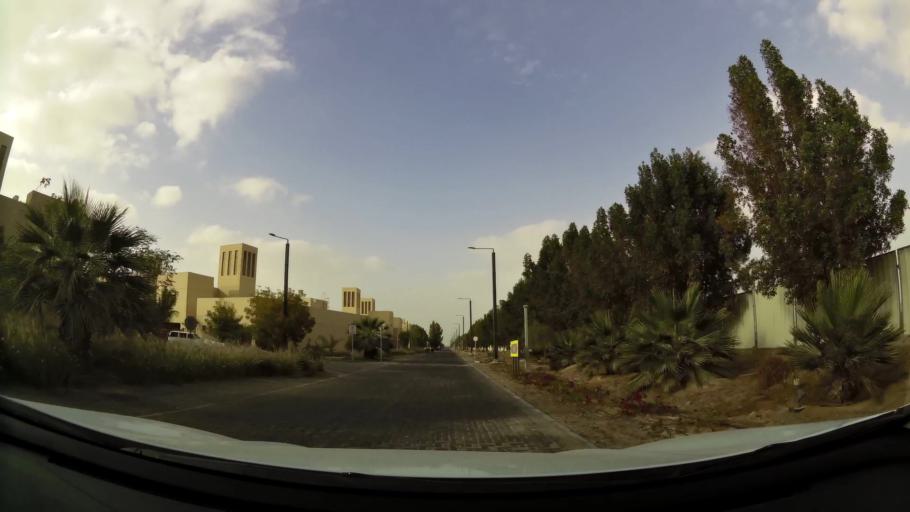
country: AE
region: Abu Dhabi
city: Abu Dhabi
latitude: 24.5053
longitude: 54.6024
